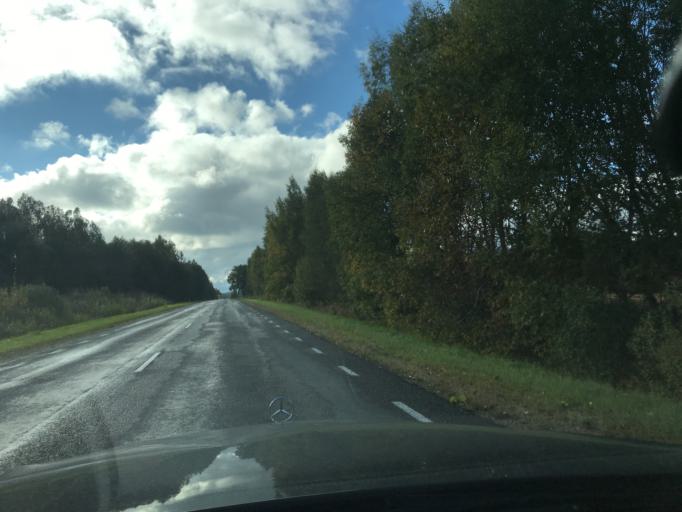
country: EE
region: Tartu
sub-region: Elva linn
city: Elva
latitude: 57.9849
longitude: 26.2619
